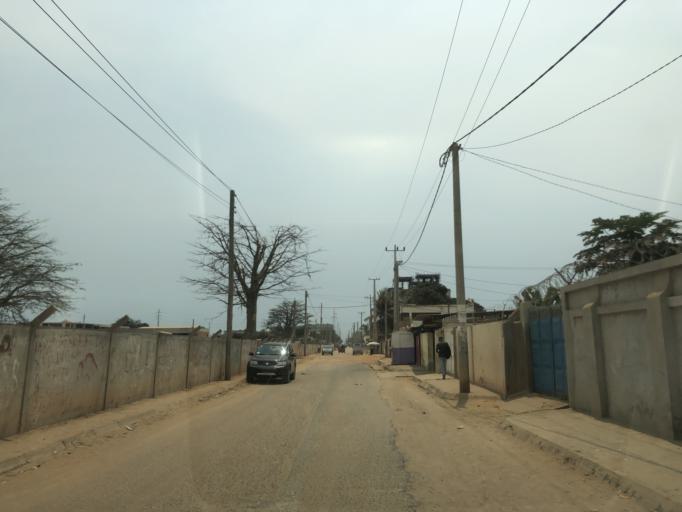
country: AO
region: Luanda
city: Luanda
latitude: -8.8882
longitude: 13.1923
